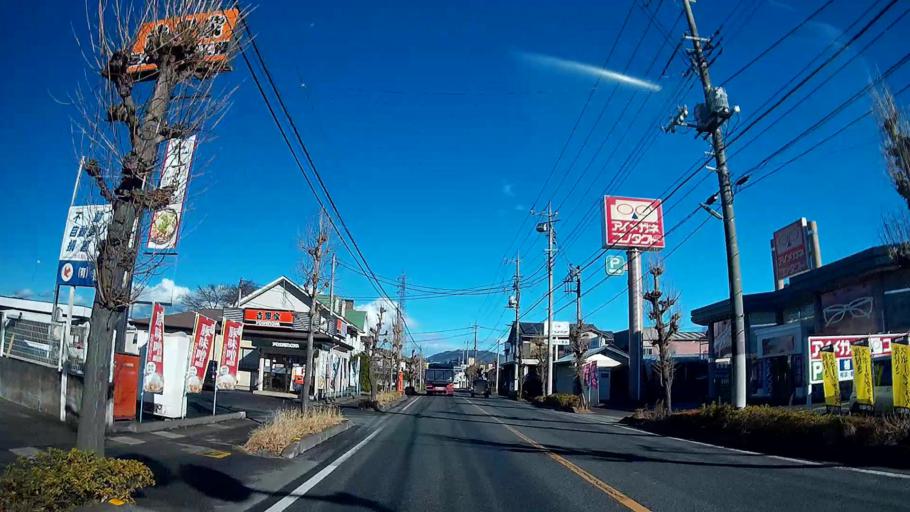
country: JP
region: Saitama
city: Chichibu
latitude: 36.0041
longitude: 139.0908
